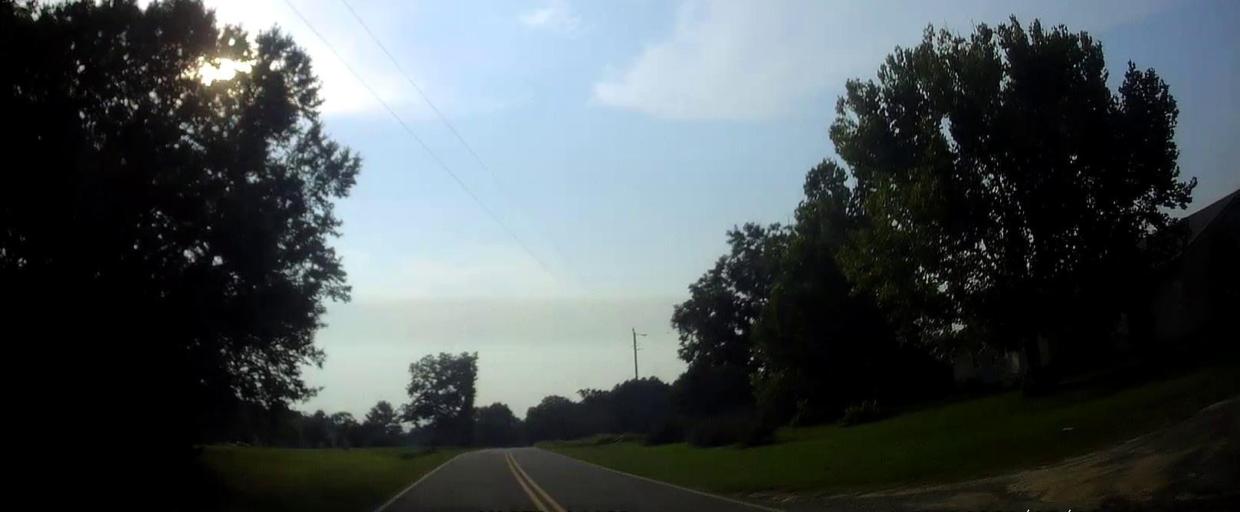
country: US
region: Georgia
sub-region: Laurens County
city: Dublin
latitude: 32.4814
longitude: -82.9649
